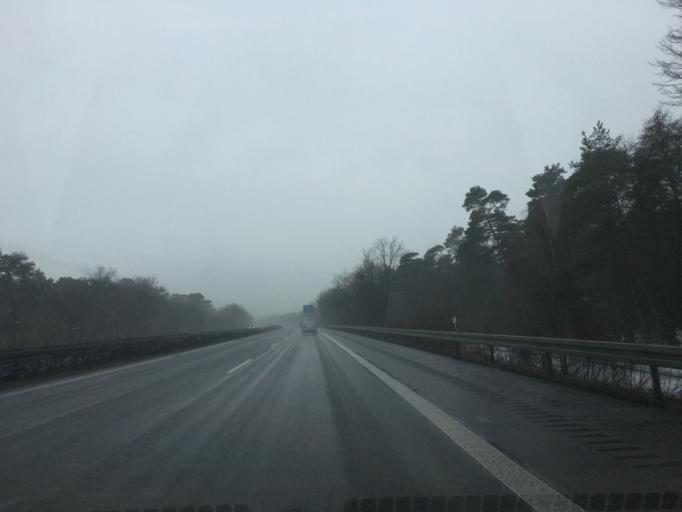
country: DE
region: North Rhine-Westphalia
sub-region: Regierungsbezirk Munster
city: Haltern
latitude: 51.7986
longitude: 7.1840
